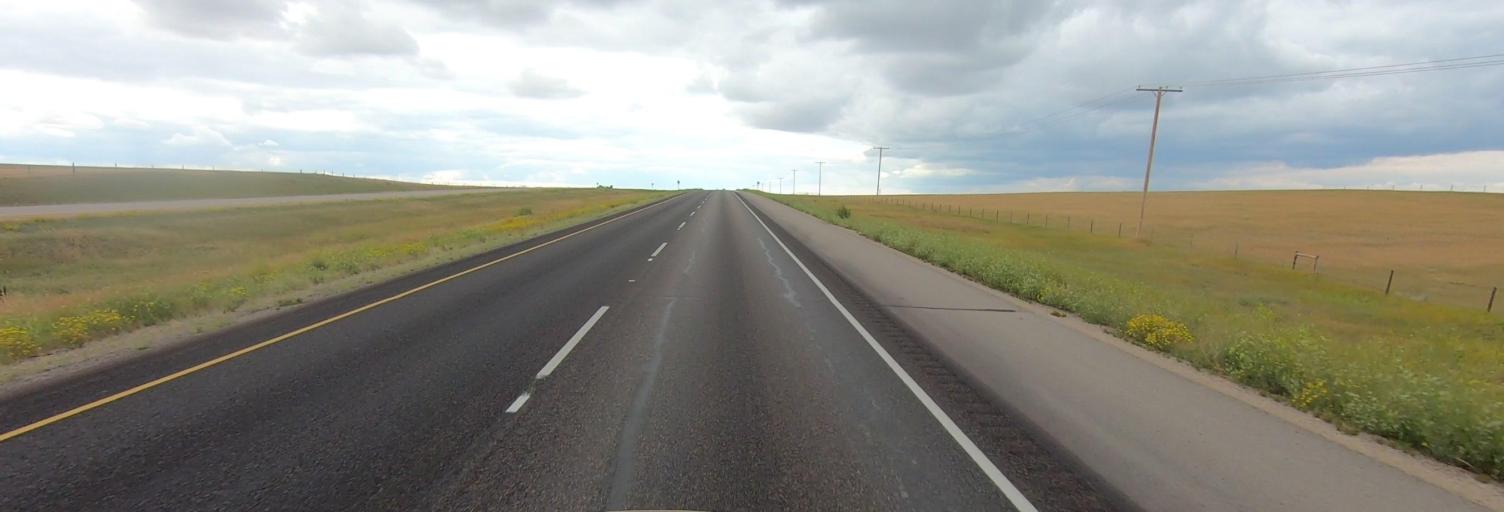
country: CA
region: Saskatchewan
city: Shaunavon
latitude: 50.0707
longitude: -108.6865
